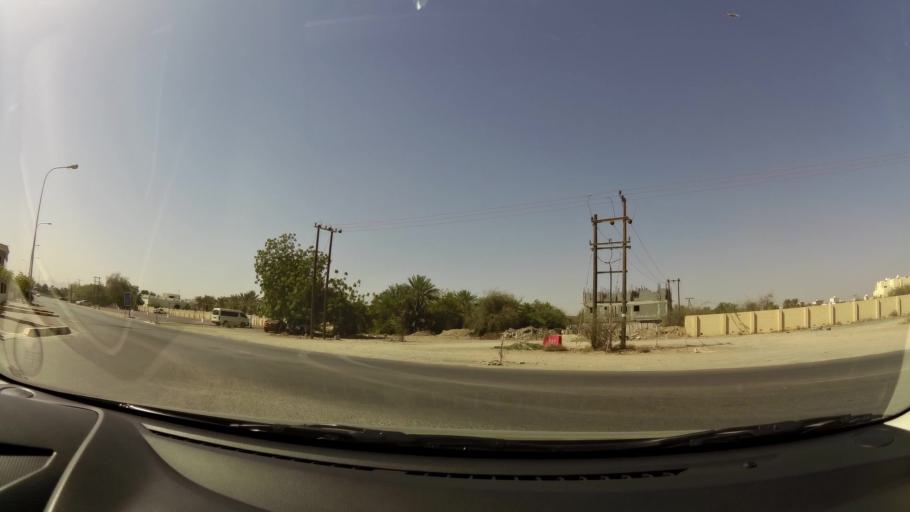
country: OM
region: Muhafazat Masqat
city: As Sib al Jadidah
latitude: 23.6092
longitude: 58.2445
